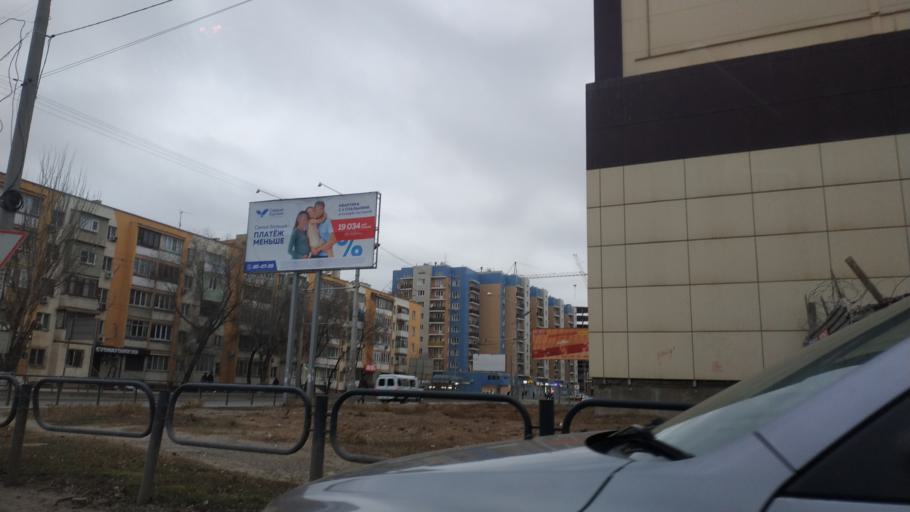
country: RU
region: Astrakhan
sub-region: Gorod Astrakhan'
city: Astrakhan'
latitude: 46.3367
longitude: 48.0221
